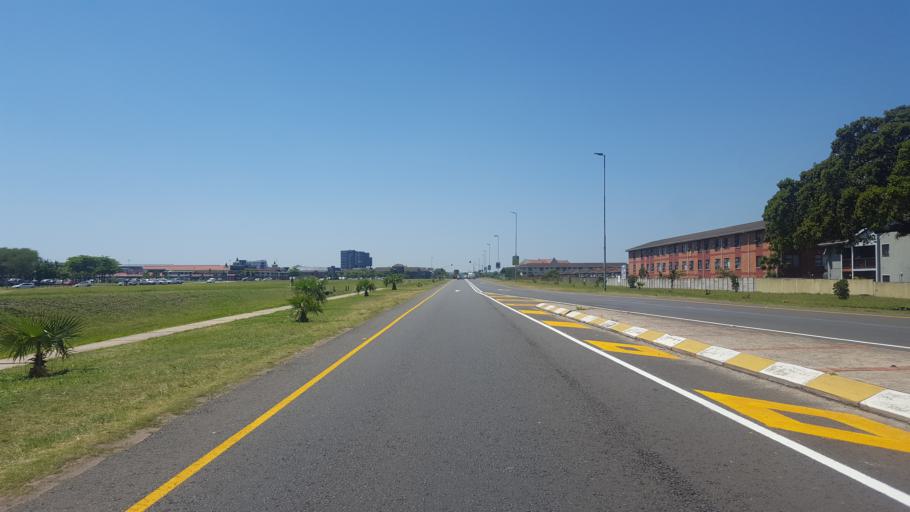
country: ZA
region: KwaZulu-Natal
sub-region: uThungulu District Municipality
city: Richards Bay
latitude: -28.7582
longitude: 32.0519
